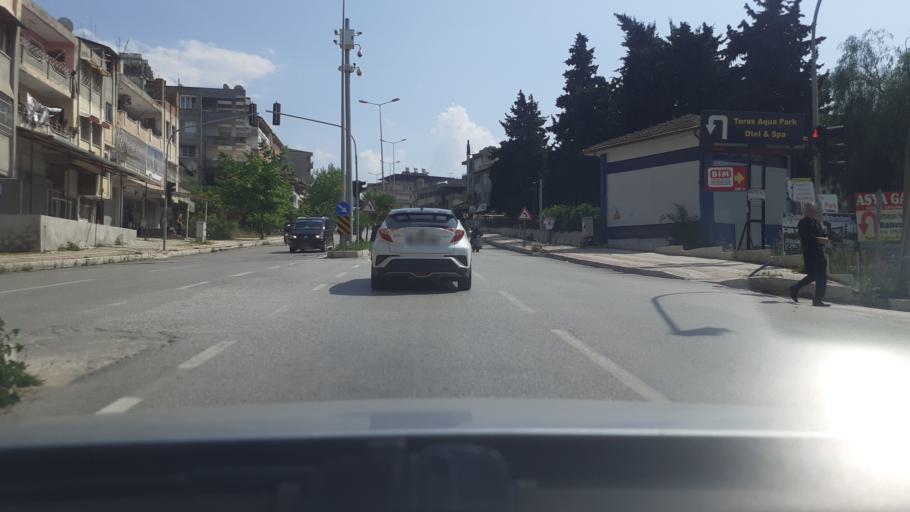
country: TR
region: Hatay
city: Gumusgoze
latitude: 36.1447
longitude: 36.1414
